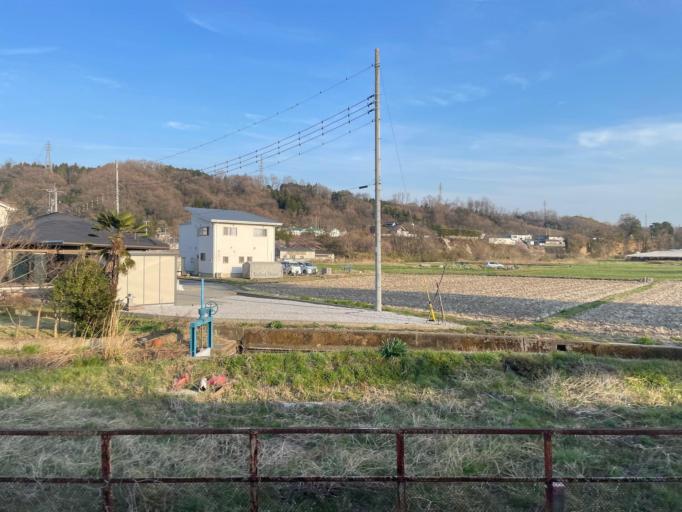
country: JP
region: Gunma
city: Annaka
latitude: 36.3278
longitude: 138.9054
